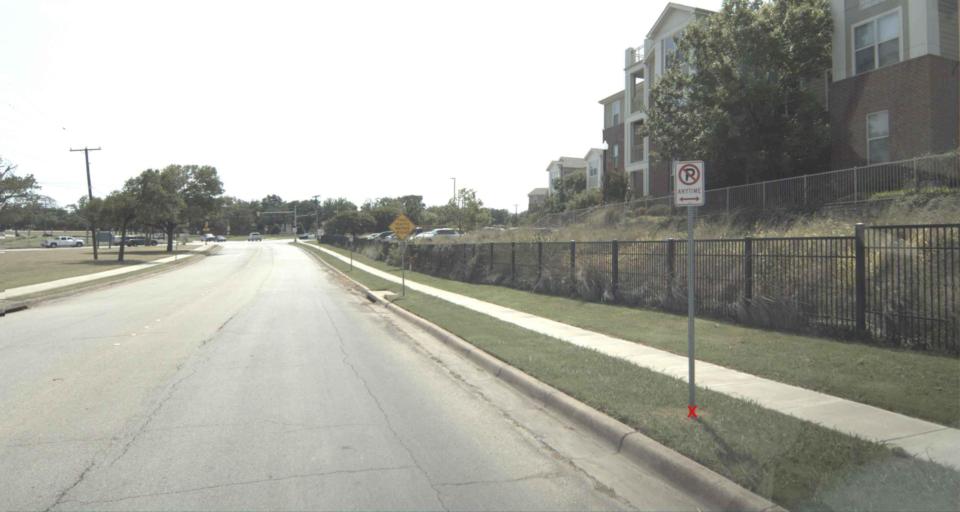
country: US
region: Texas
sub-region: Tarrant County
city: Edgecliff Village
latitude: 32.6858
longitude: -97.3440
